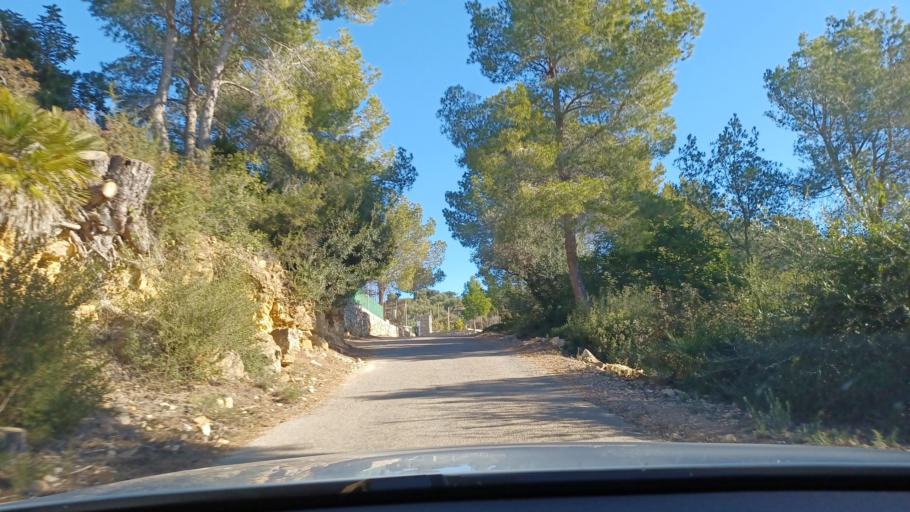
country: ES
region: Catalonia
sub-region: Provincia de Tarragona
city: Tortosa
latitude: 40.8141
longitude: 0.5554
